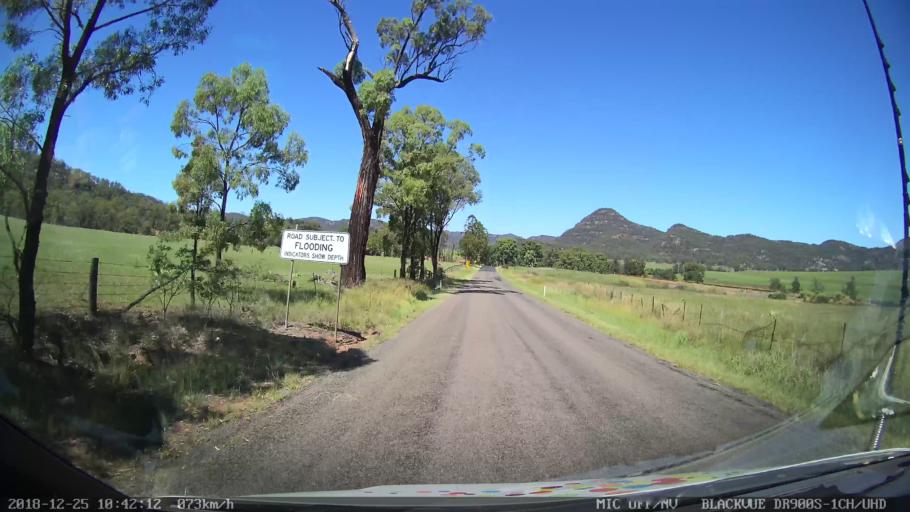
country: AU
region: New South Wales
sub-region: Upper Hunter Shire
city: Merriwa
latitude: -32.4149
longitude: 150.3265
